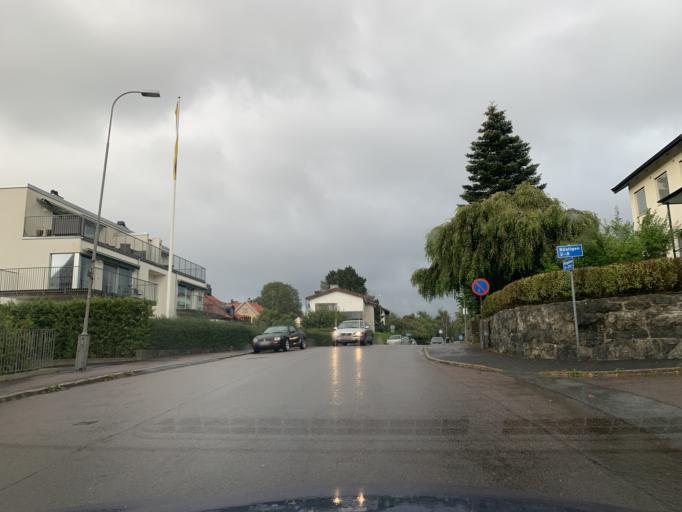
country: SE
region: Vaestra Goetaland
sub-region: Goteborg
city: Goeteborg
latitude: 57.7019
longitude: 12.0080
